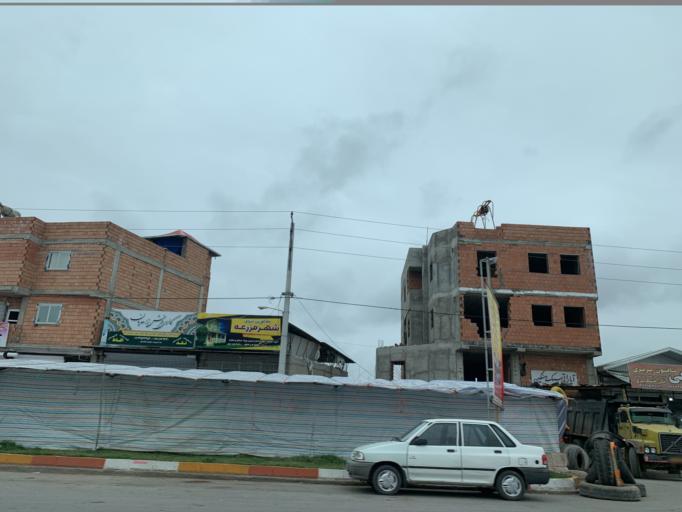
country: IR
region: Mazandaran
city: Babol
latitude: 36.5154
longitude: 52.5699
